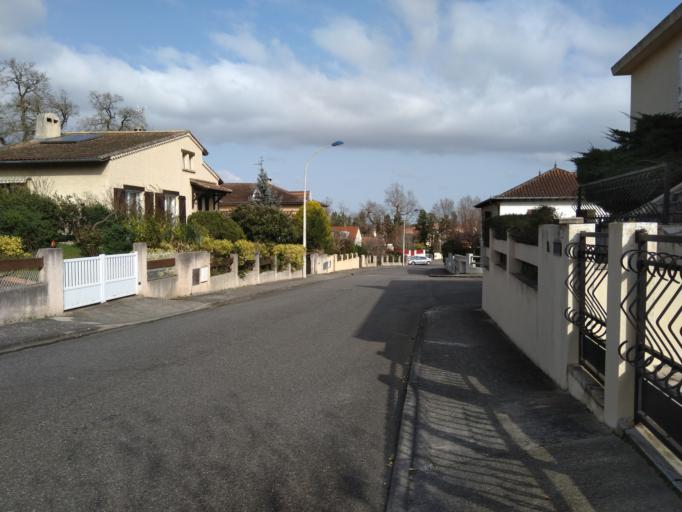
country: FR
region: Midi-Pyrenees
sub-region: Departement de la Haute-Garonne
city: Ramonville-Saint-Agne
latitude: 43.5469
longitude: 1.4634
